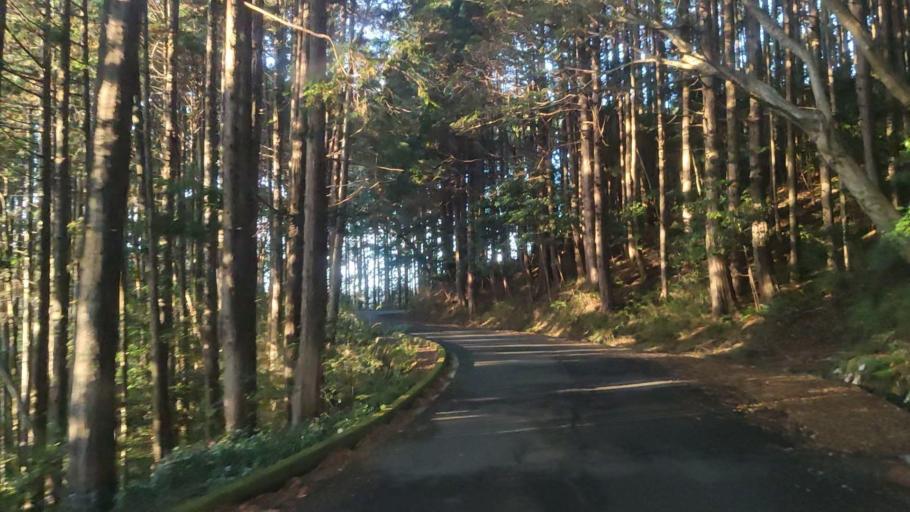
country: JP
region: Kanagawa
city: Yugawara
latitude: 35.1252
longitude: 139.0197
